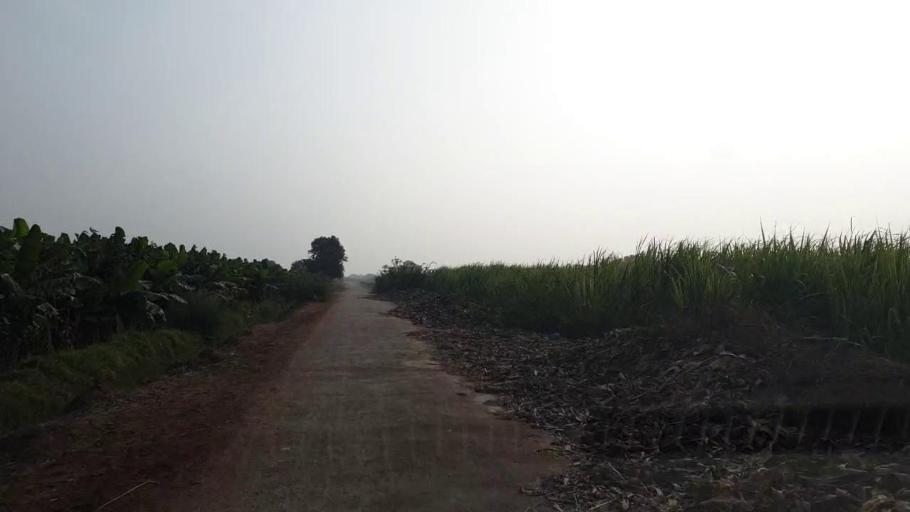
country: PK
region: Sindh
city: Tando Muhammad Khan
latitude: 25.1614
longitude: 68.5886
